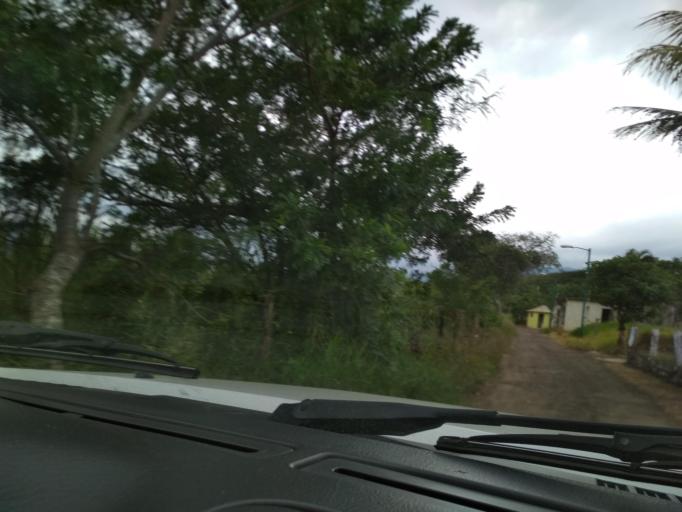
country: MX
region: Veracruz
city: El Castillo
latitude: 19.5857
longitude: -96.8409
